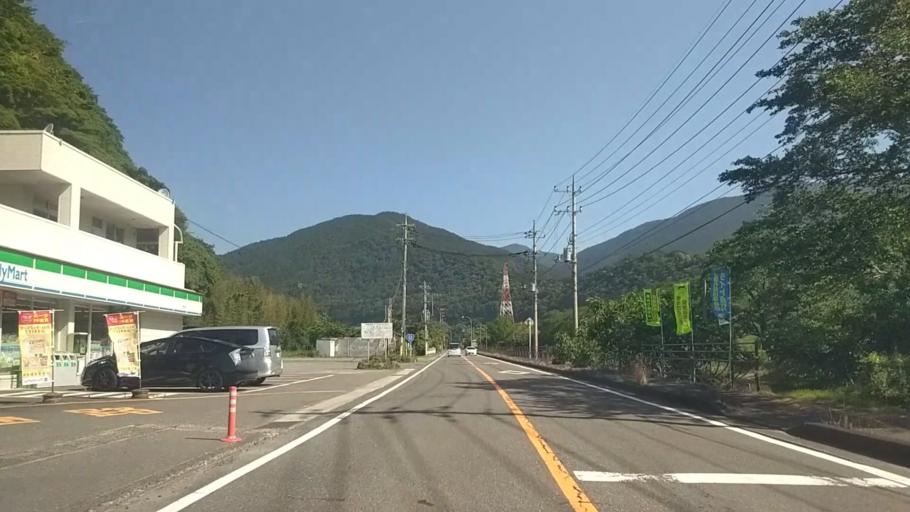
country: JP
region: Shizuoka
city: Fujinomiya
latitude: 35.2321
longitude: 138.5074
